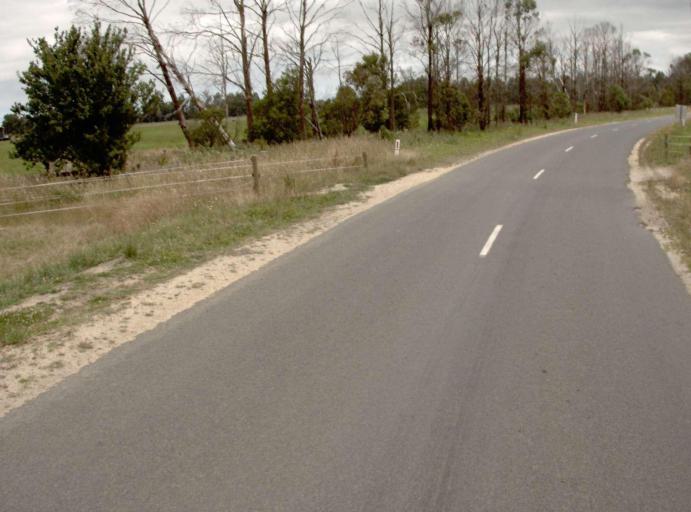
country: AU
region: Victoria
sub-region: Latrobe
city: Traralgon
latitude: -38.4972
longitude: 146.6780
